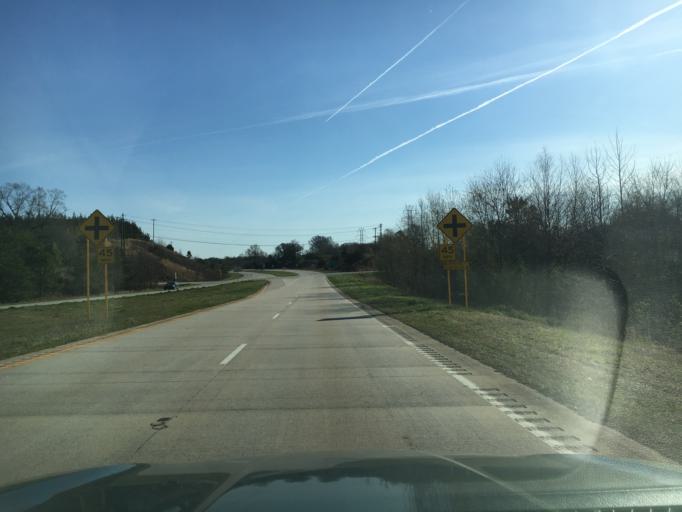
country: US
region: South Carolina
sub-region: Greenville County
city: Greer
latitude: 34.9243
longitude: -82.1965
